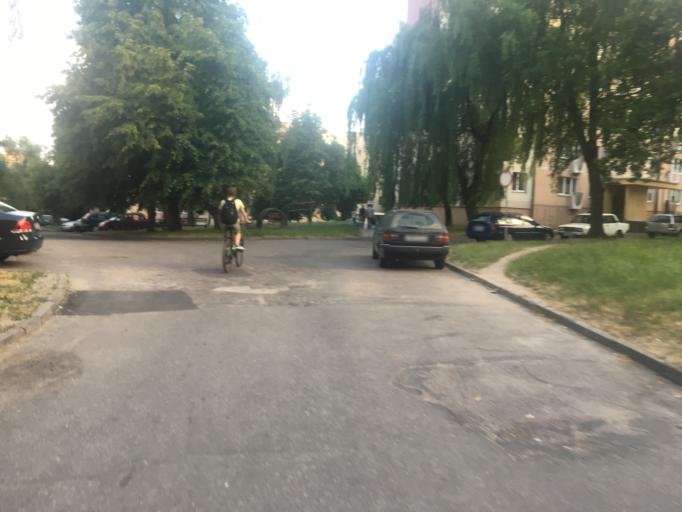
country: BY
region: Grodnenskaya
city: Hrodna
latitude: 53.6958
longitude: 23.8084
